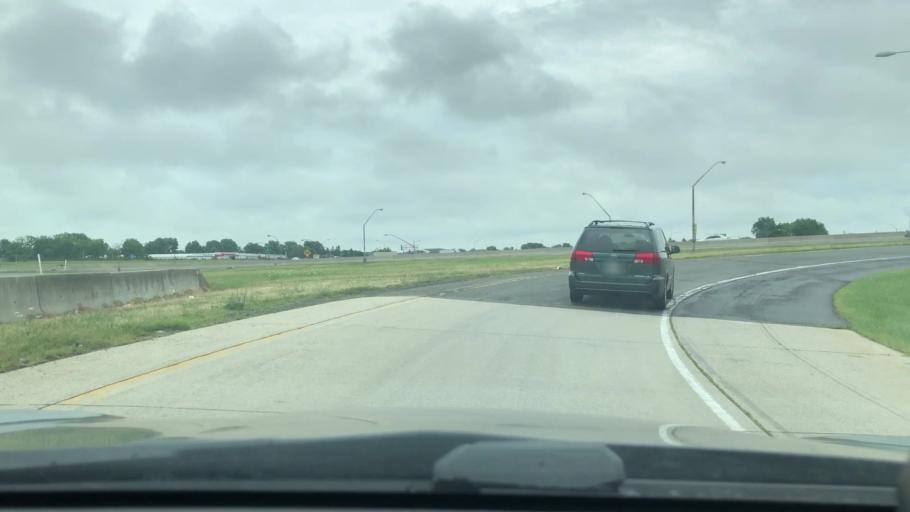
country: US
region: Pennsylvania
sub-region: Lehigh County
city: Fullerton
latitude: 40.6445
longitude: -75.4324
